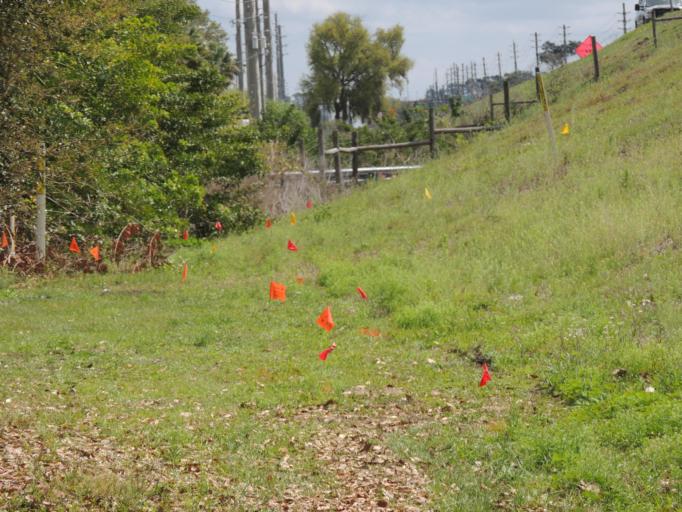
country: US
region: Florida
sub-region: Osceola County
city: Buenaventura Lakes
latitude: 28.3038
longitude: -81.3638
